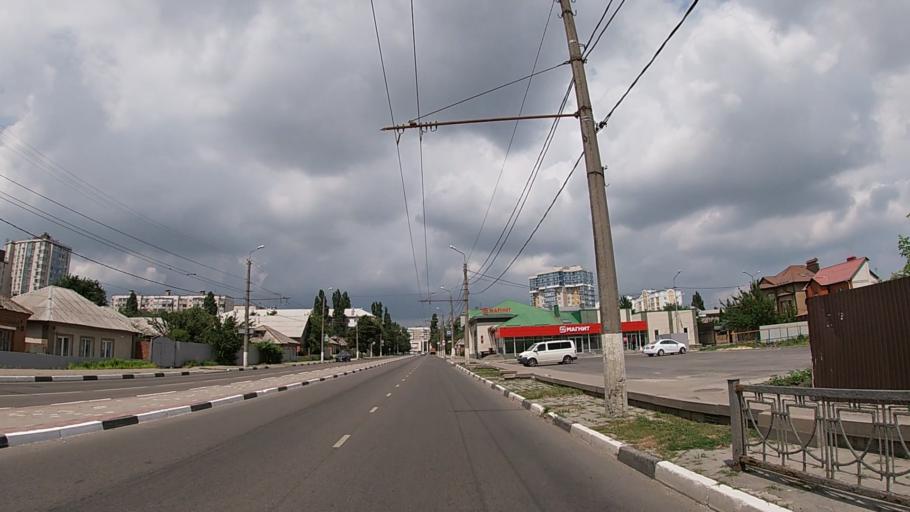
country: RU
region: Belgorod
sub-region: Belgorodskiy Rayon
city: Belgorod
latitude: 50.6096
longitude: 36.5920
